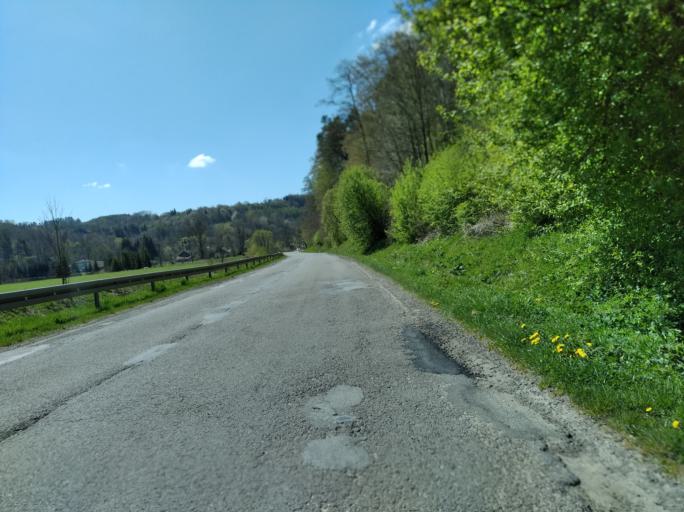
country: PL
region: Subcarpathian Voivodeship
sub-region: Powiat brzozowski
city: Dydnia
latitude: 49.7008
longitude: 22.1934
